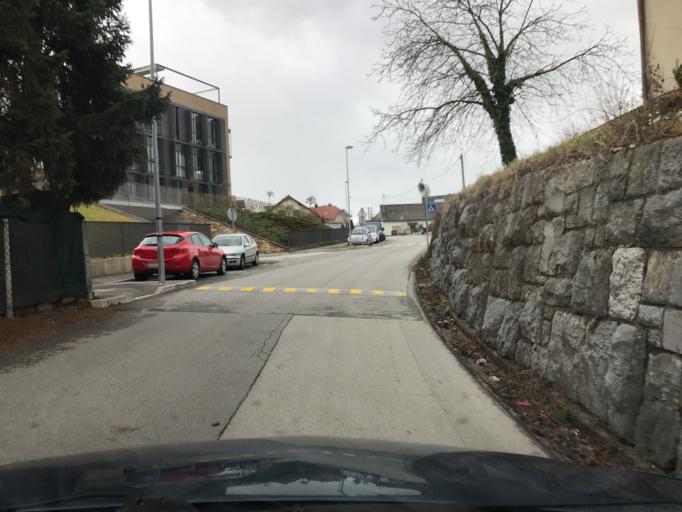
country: SI
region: Ljubljana
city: Ljubljana
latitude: 46.0853
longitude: 14.5162
